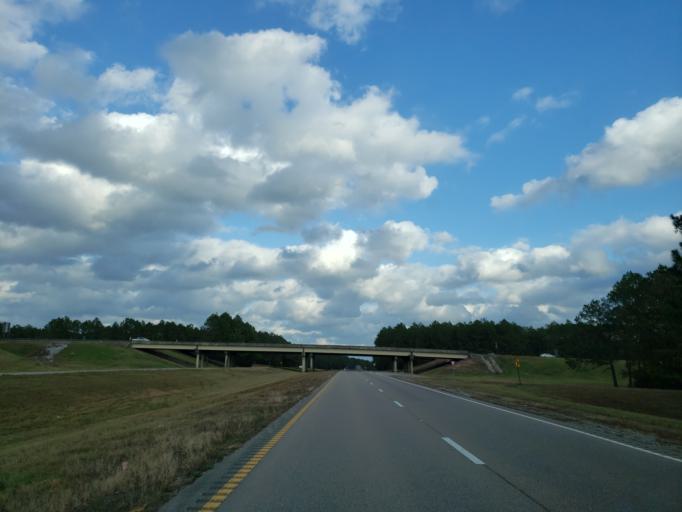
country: US
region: Mississippi
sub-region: Forrest County
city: Hattiesburg
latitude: 31.2439
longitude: -89.2778
